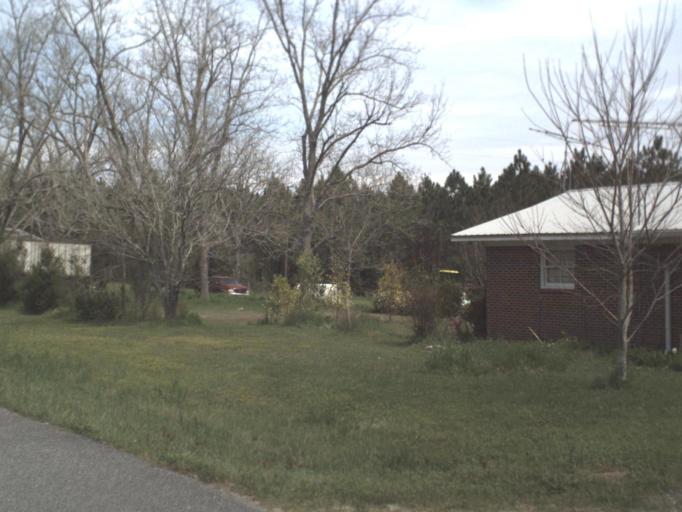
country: US
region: Florida
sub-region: Washington County
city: Chipley
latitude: 30.8383
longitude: -85.5018
